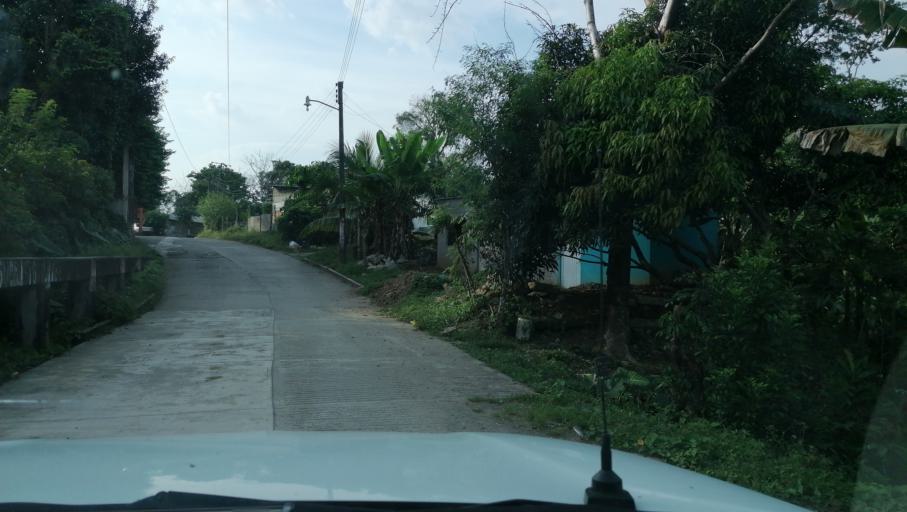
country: MX
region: Chiapas
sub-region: Juarez
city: El Triunfo 1ra. Seccion (Cardona)
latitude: 17.4873
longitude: -93.2430
